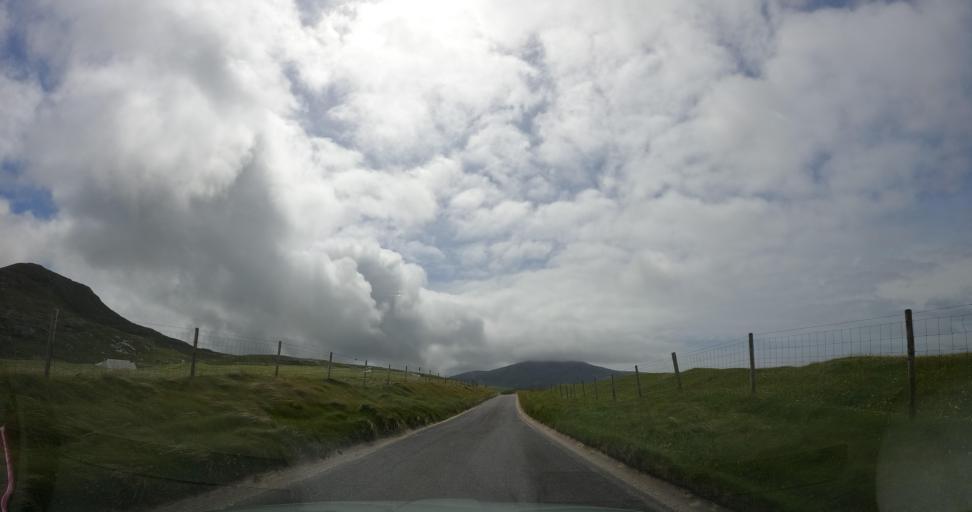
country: GB
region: Scotland
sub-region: Eilean Siar
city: Barra
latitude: 56.9961
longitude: -7.5067
